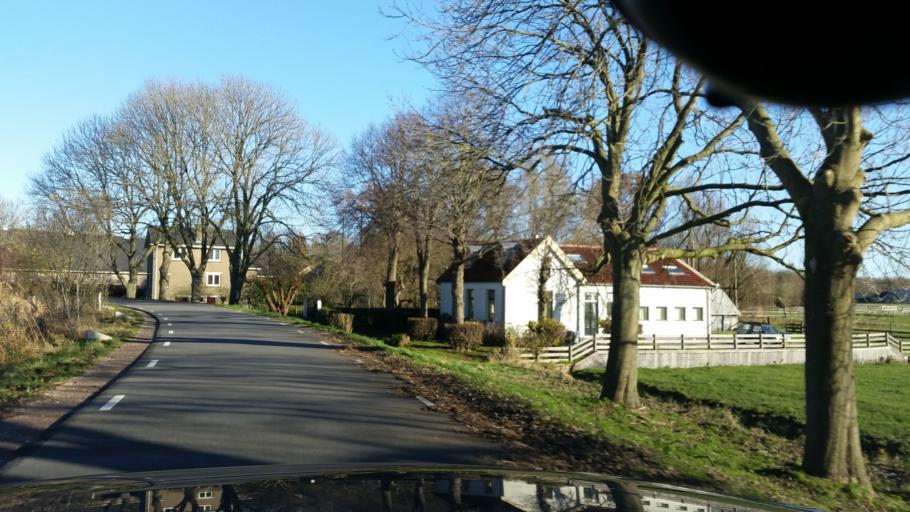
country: NL
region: North Holland
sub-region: Gemeente Ouder-Amstel
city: Ouderkerk aan de Amstel
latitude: 52.2911
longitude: 4.8909
